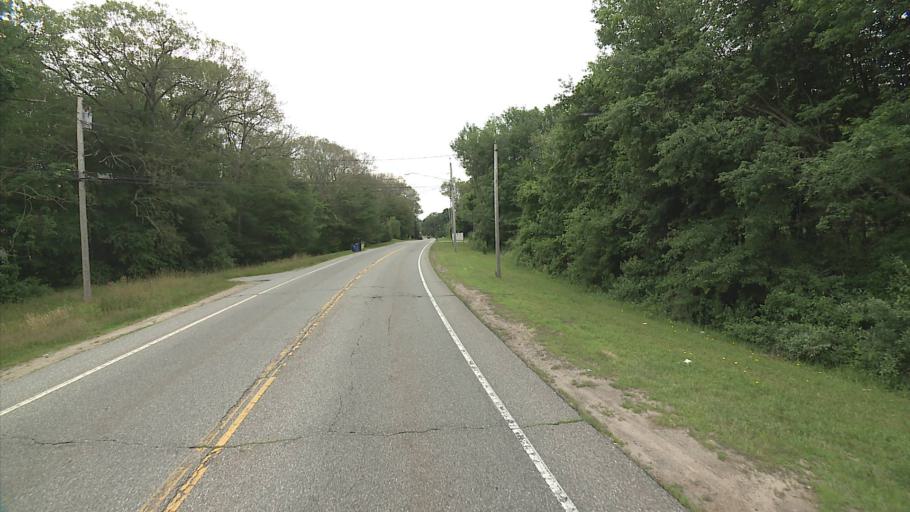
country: US
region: Connecticut
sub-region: New London County
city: Conning Towers-Nautilus Park
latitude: 41.3928
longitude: -72.0271
